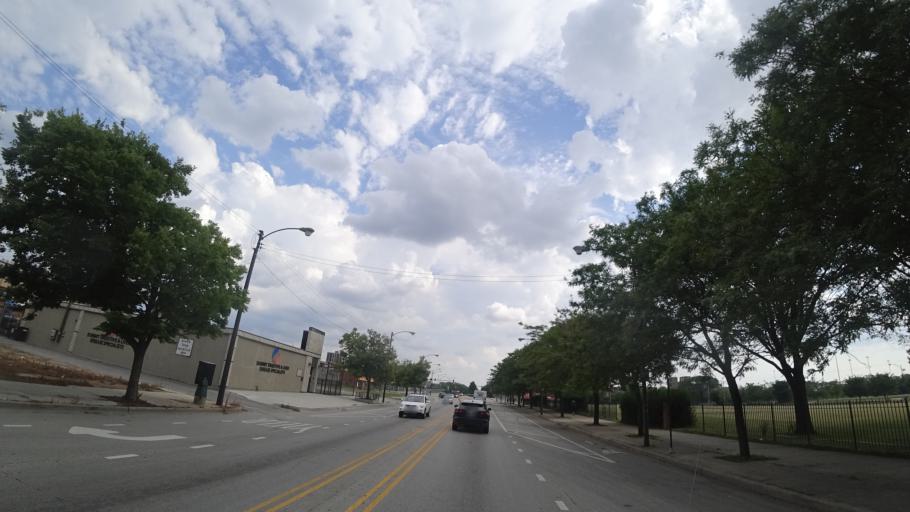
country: US
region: Illinois
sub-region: Cook County
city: Chicago
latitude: 41.8491
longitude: -87.6270
